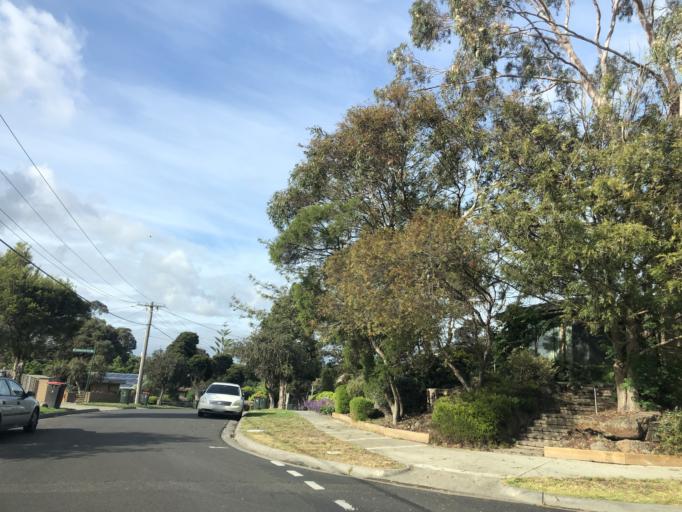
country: AU
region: Victoria
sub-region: Monash
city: Ashwood
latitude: -37.8638
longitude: 145.1001
